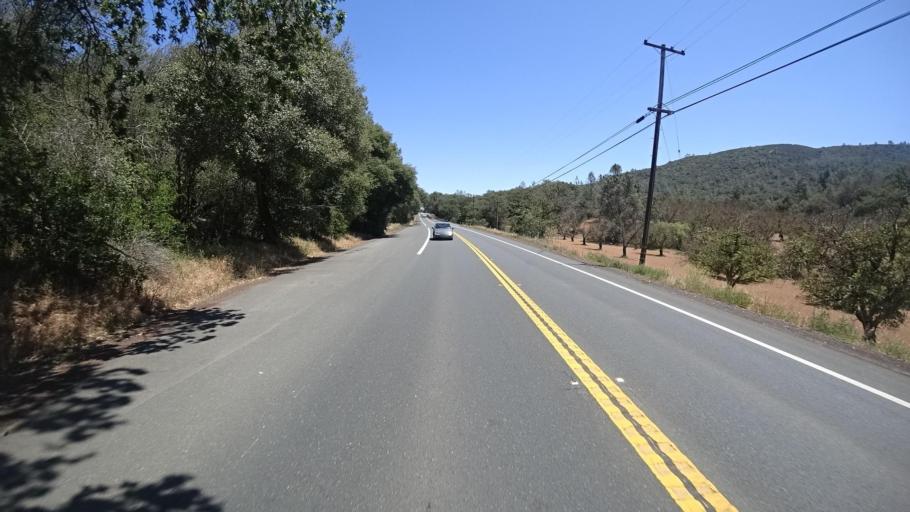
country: US
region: California
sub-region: Lake County
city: Clearlake Oaks
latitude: 39.0139
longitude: -122.6358
